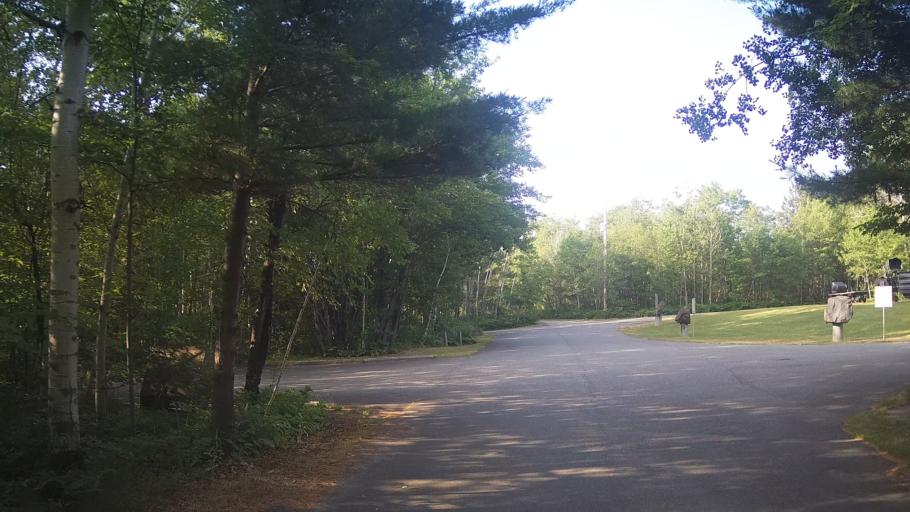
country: CA
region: Ontario
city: Rayside-Balfour
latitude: 46.5882
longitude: -81.3804
